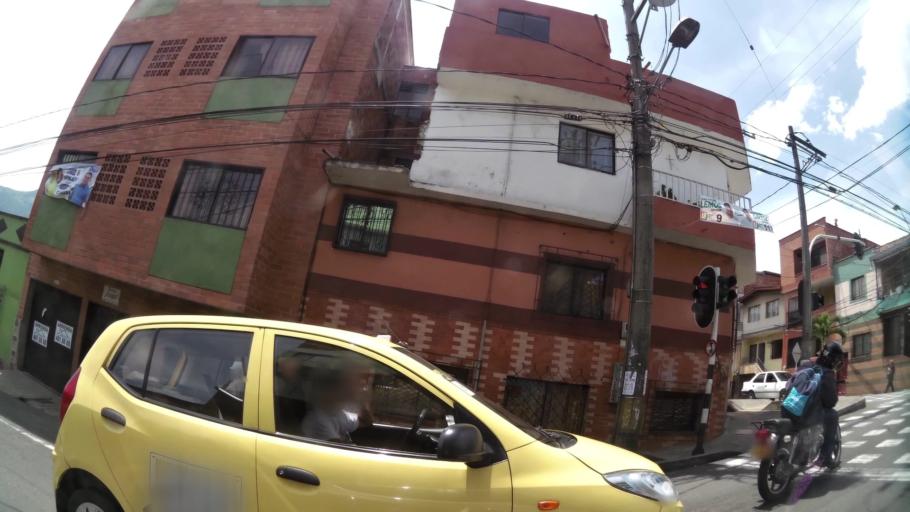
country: CO
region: Antioquia
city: Bello
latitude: 6.3385
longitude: -75.5580
